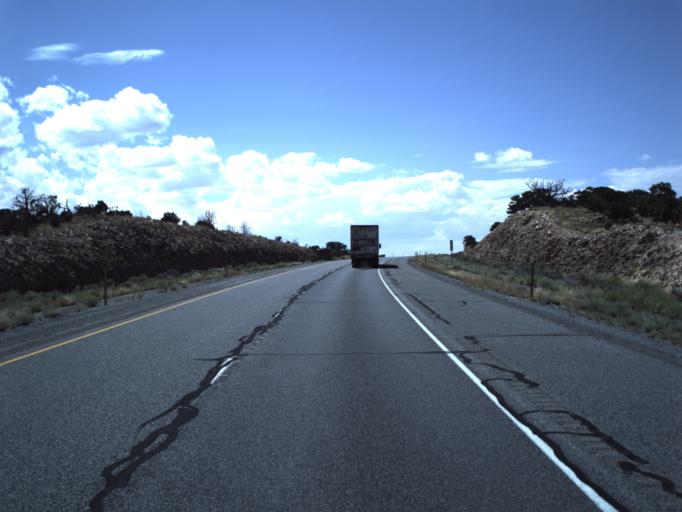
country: US
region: Utah
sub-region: Emery County
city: Castle Dale
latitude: 38.8982
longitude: -110.5794
